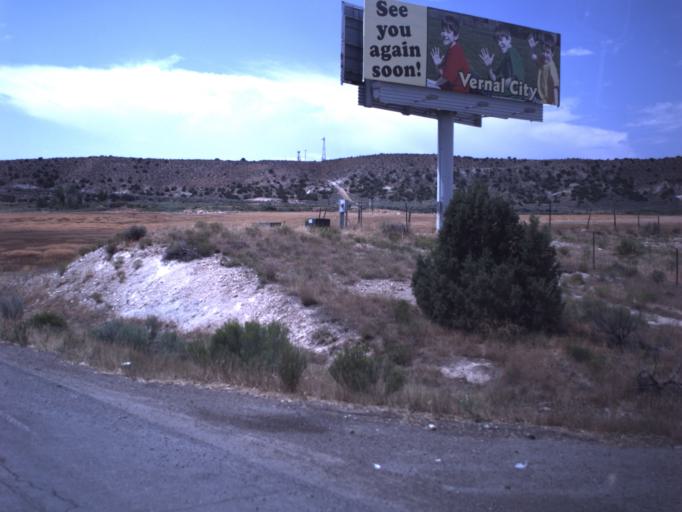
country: US
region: Utah
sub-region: Uintah County
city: Maeser
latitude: 40.4228
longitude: -109.5805
